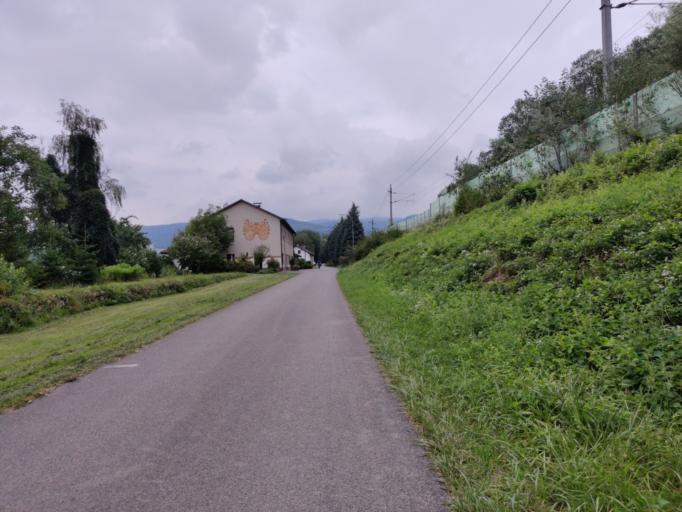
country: AT
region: Lower Austria
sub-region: Politischer Bezirk Melk
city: Ybbs an der Donau
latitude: 48.1856
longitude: 15.1182
